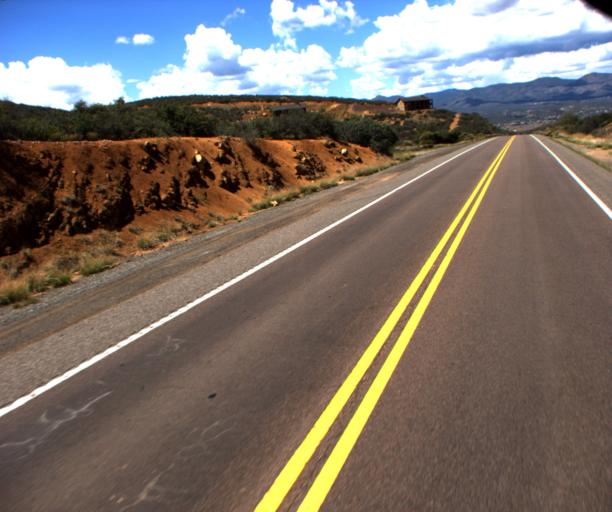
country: US
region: Arizona
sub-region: Yavapai County
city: Dewey-Humboldt
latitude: 34.5437
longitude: -112.1859
